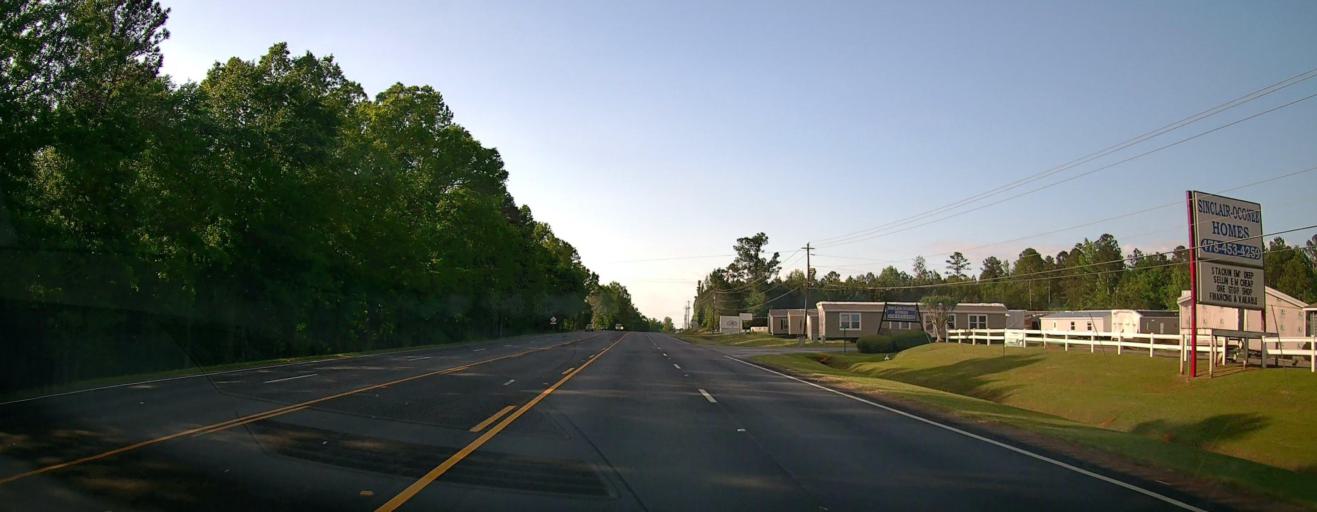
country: US
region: Georgia
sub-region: Baldwin County
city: Milledgeville
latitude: 33.1426
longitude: -83.2713
